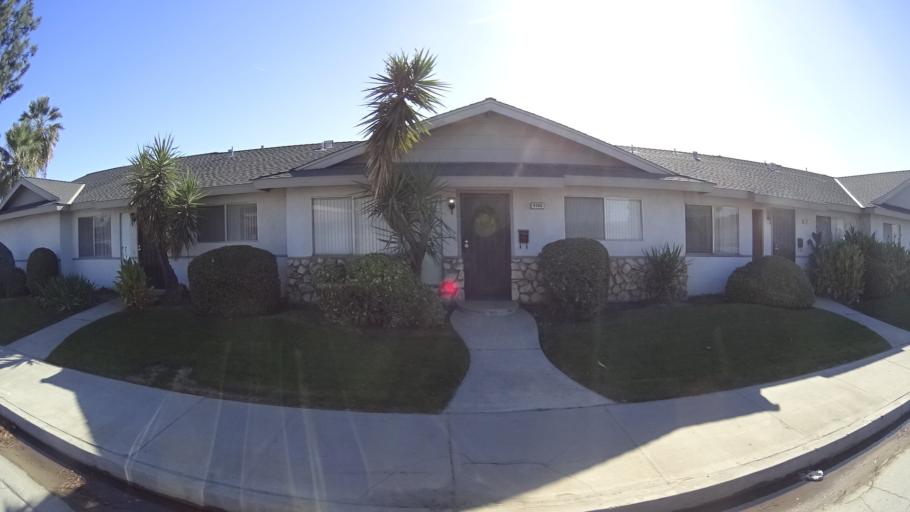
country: US
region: California
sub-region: Kern County
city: Bakersfield
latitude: 35.3658
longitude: -119.0534
